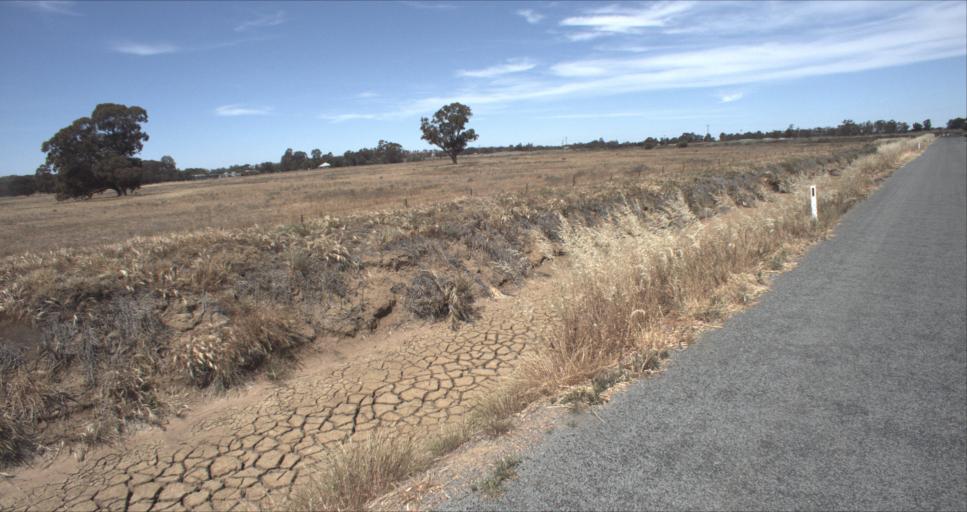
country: AU
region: New South Wales
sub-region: Leeton
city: Leeton
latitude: -34.6045
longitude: 146.4150
